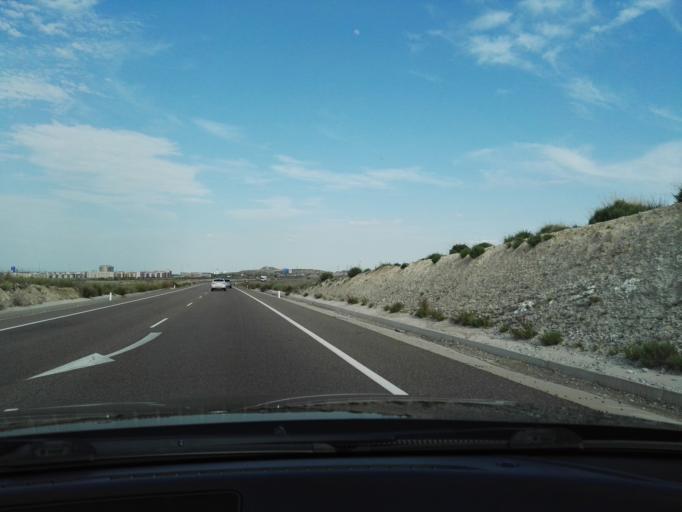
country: ES
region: Aragon
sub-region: Provincia de Zaragoza
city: Montecanal
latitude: 41.6215
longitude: -0.9769
